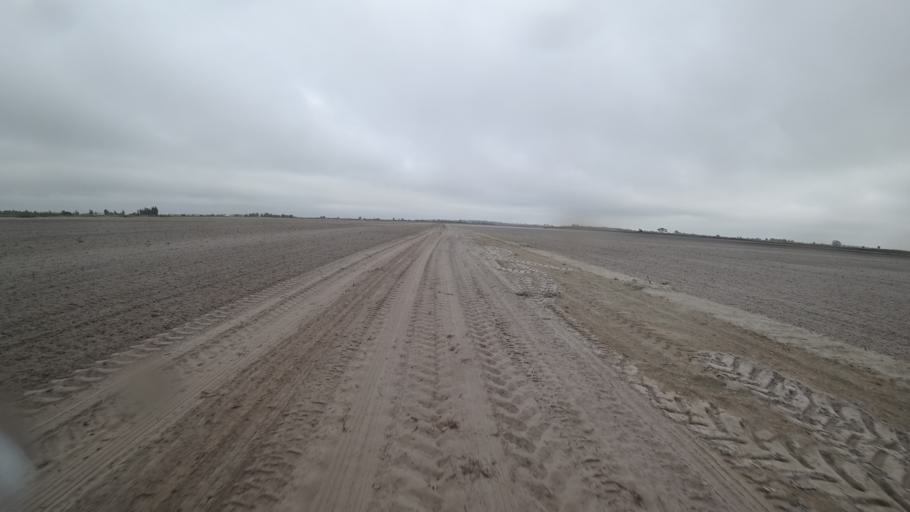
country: US
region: Florida
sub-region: Sarasota County
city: Warm Mineral Springs
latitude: 27.2877
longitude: -82.1754
